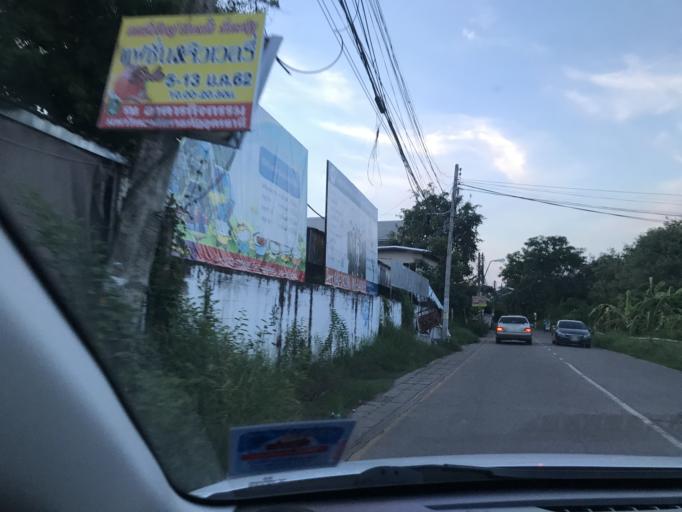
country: TH
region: Changwat Udon Thani
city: Udon Thani
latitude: 17.3960
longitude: 102.7884
